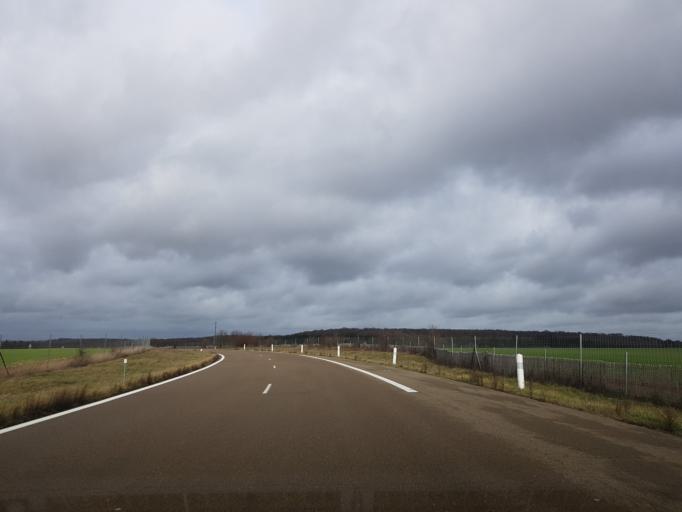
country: FR
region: Champagne-Ardenne
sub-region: Departement de la Haute-Marne
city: Rolampont
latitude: 47.9113
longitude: 5.2283
